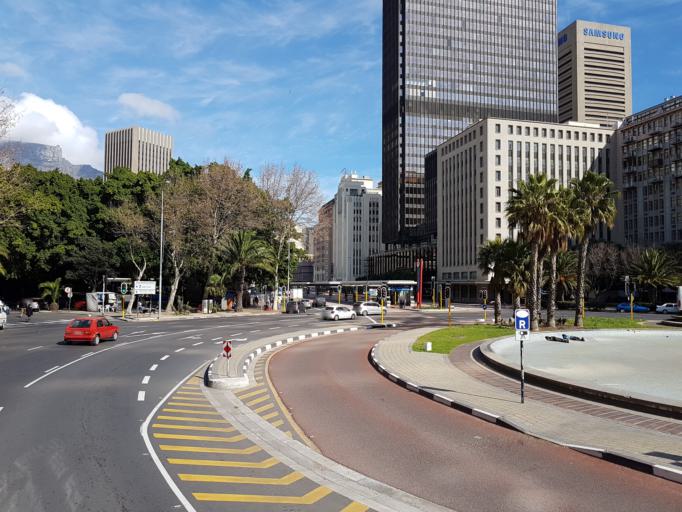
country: ZA
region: Western Cape
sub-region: City of Cape Town
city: Cape Town
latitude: -33.9199
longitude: 18.4260
